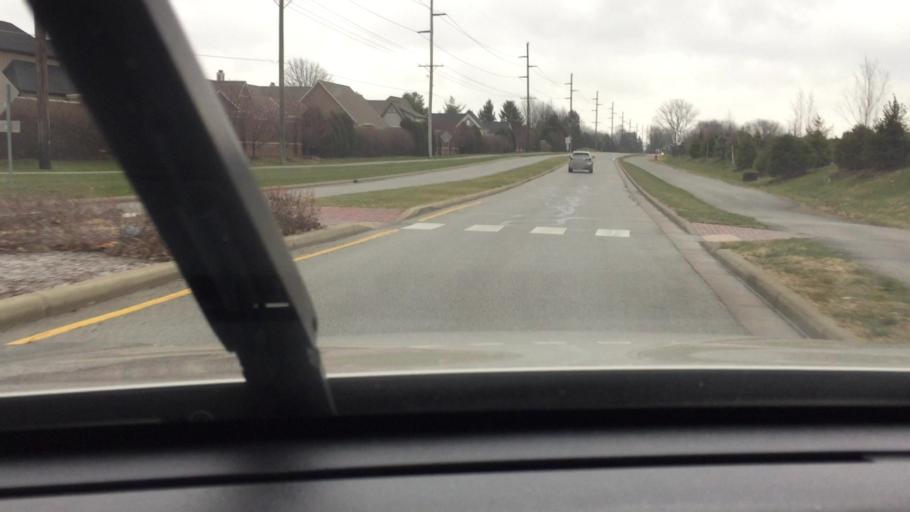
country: US
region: Indiana
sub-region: Hamilton County
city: Carmel
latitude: 40.0075
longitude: -86.1084
